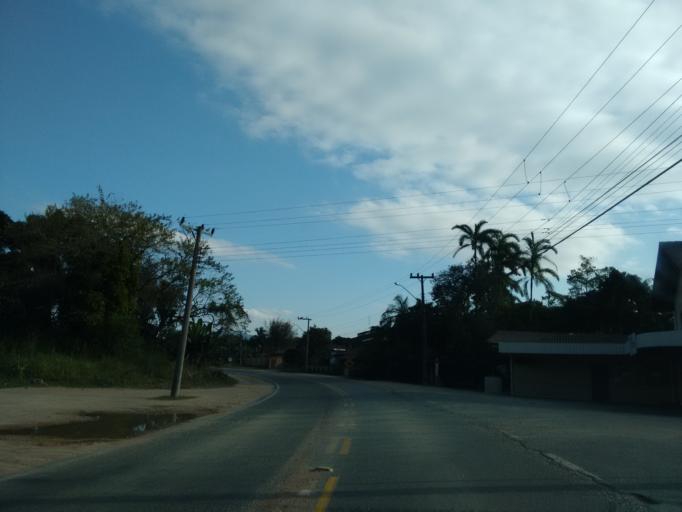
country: BR
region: Santa Catarina
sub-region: Pomerode
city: Pomerode
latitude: -26.6793
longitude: -49.1461
